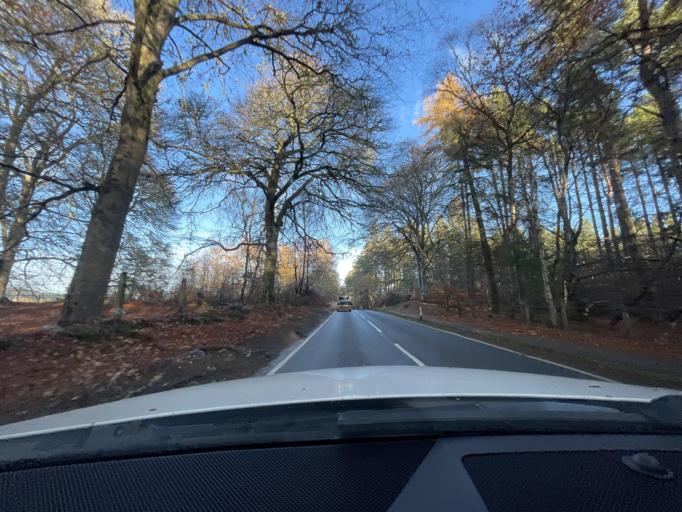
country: GB
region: Scotland
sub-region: Highland
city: Inverness
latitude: 57.4377
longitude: -4.2665
